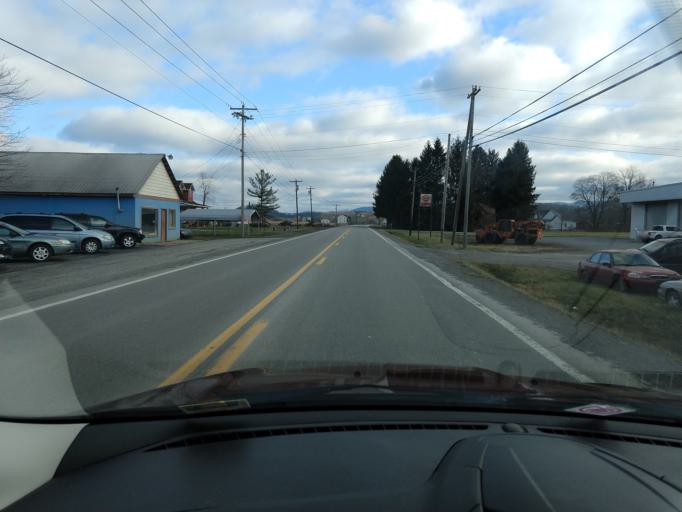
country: US
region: West Virginia
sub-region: Randolph County
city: Elkins
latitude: 38.8016
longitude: -79.8920
